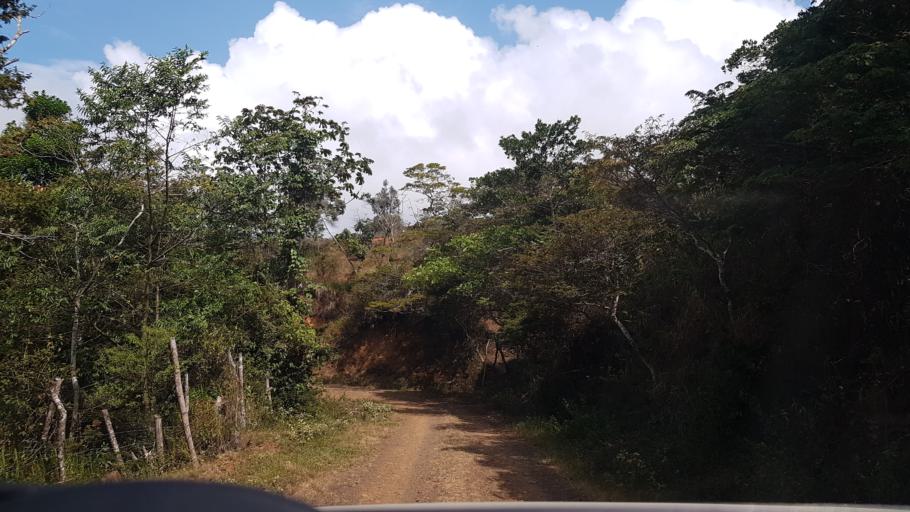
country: CO
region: Valle del Cauca
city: Yumbo
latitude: 3.6542
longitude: -76.5178
